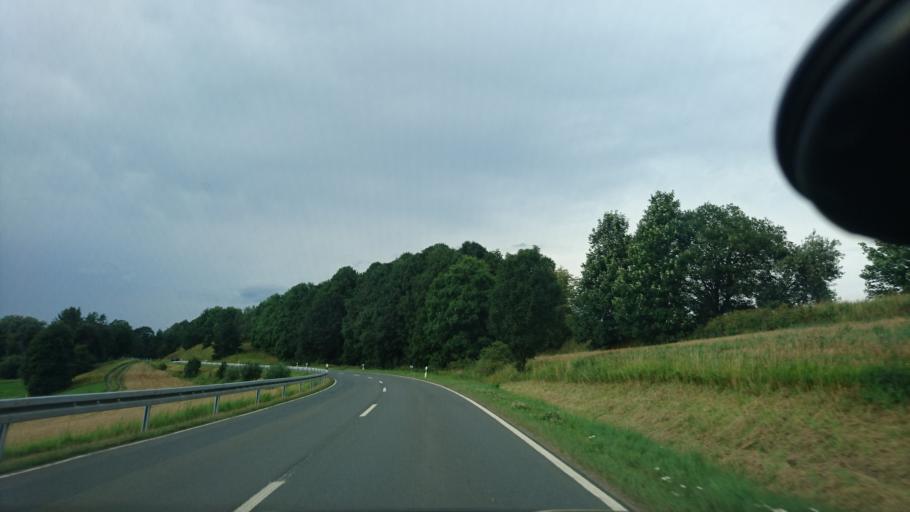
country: DE
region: Bavaria
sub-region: Upper Franconia
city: Selbitz
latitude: 50.3048
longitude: 11.7465
